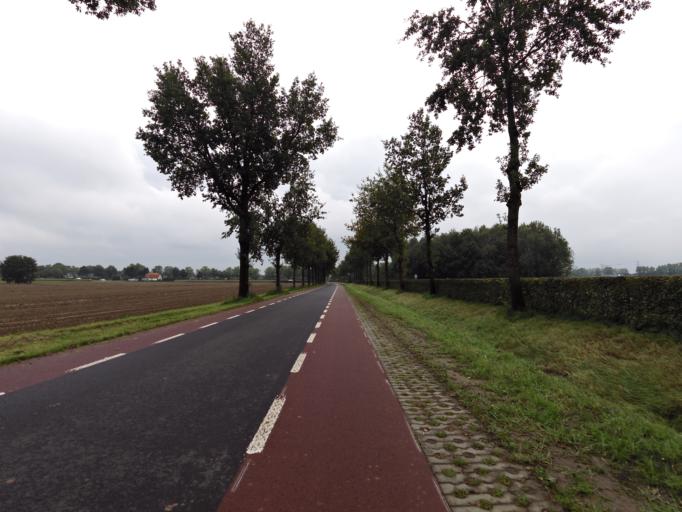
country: NL
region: Gelderland
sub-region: Gemeente Doetinchem
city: Doetinchem
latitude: 51.9213
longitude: 6.3249
